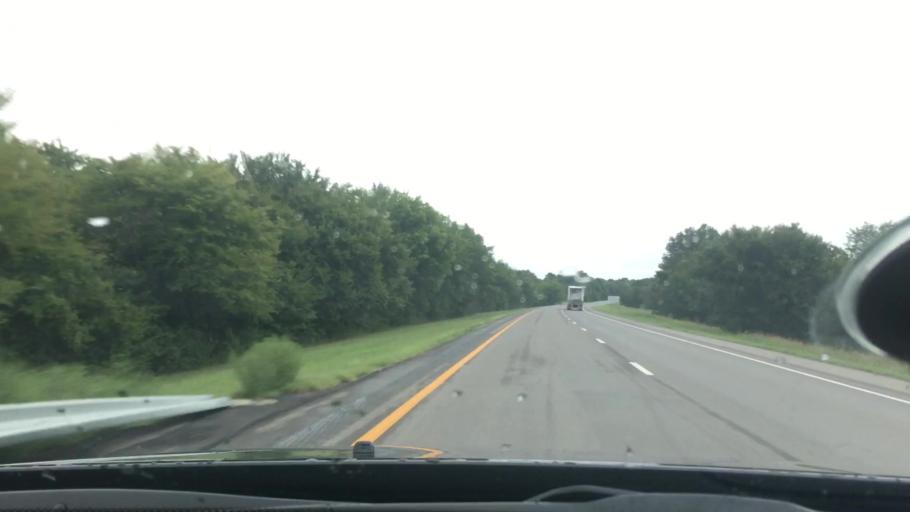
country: US
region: Oklahoma
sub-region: Okmulgee County
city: Morris
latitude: 35.4460
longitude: -95.7674
